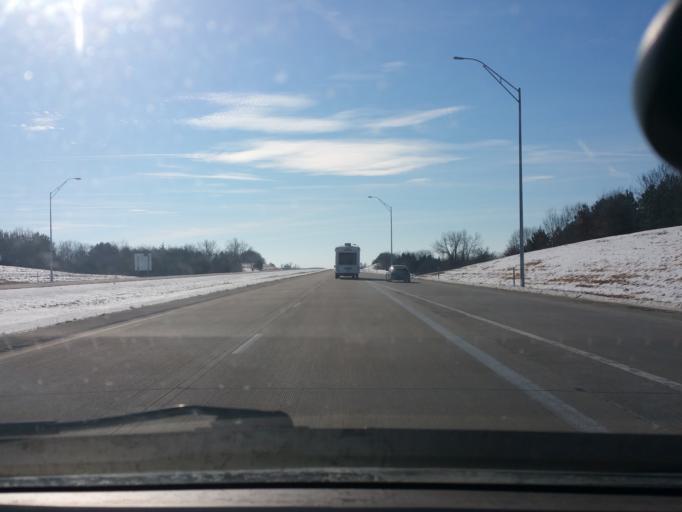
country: US
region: Iowa
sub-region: Decatur County
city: Leon
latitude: 40.7347
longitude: -93.8433
